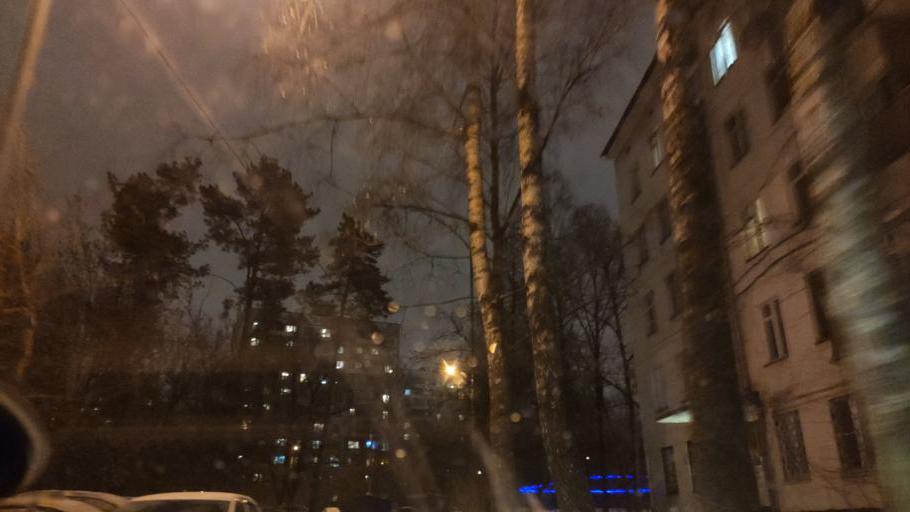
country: RU
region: Moscow
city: Kotlovka
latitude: 55.6645
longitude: 37.5884
